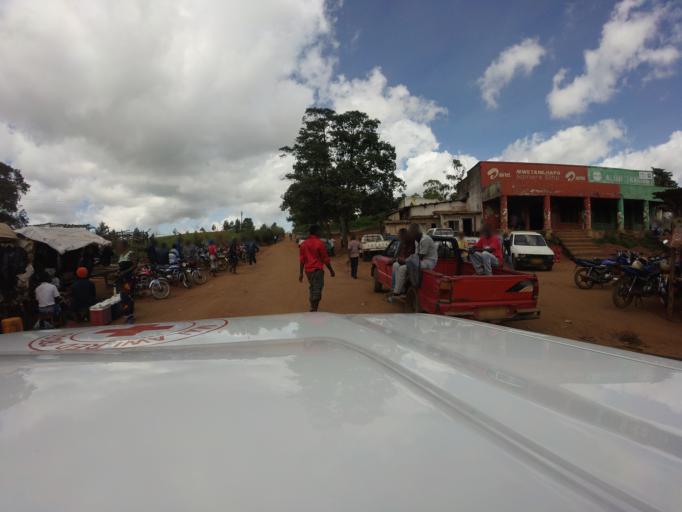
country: MW
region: Southern Region
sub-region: Thyolo District
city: Thyolo
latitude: -15.9891
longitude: 35.0784
